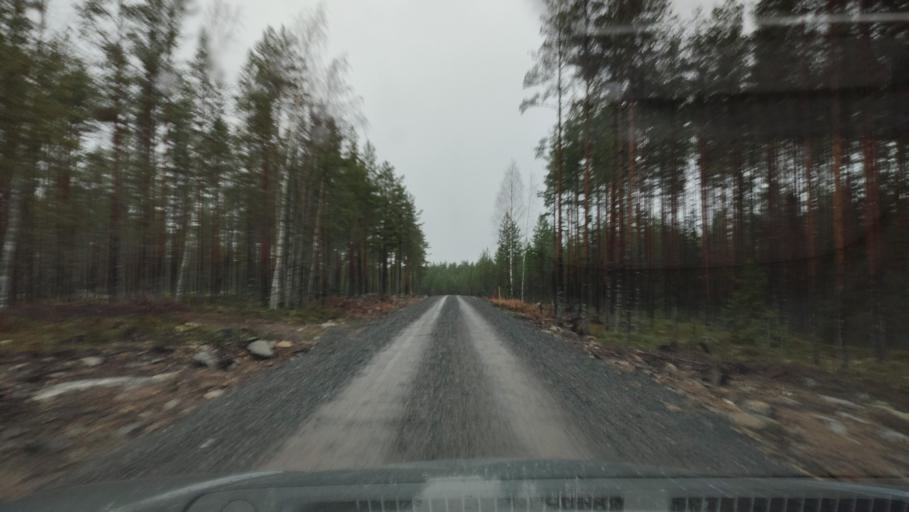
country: FI
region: Southern Ostrobothnia
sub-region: Suupohja
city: Karijoki
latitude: 62.1463
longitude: 21.6263
